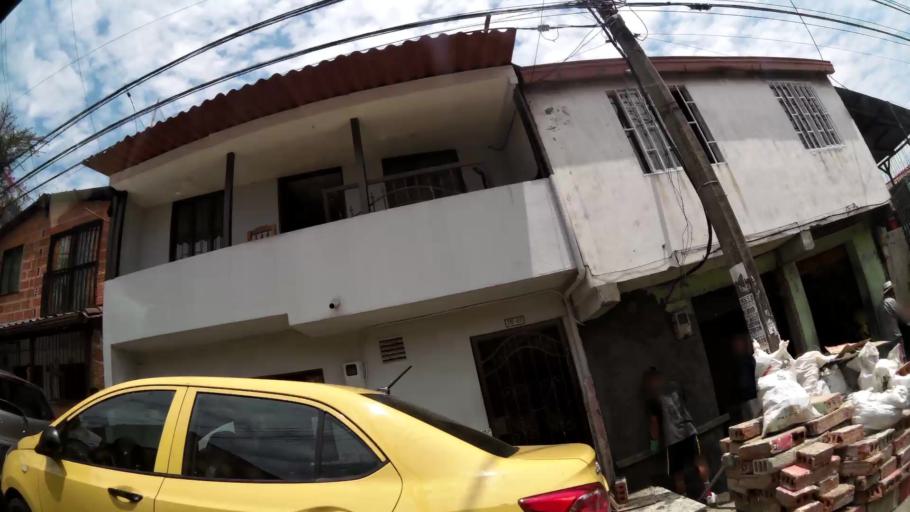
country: CO
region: Antioquia
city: Bello
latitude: 6.3143
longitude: -75.5822
